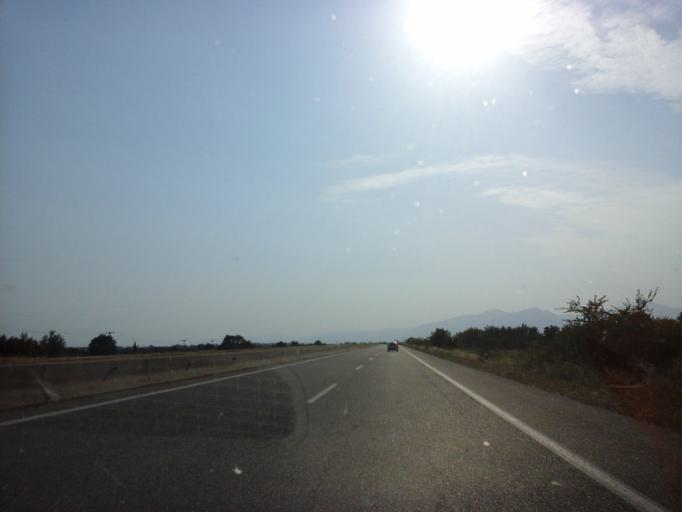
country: GR
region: East Macedonia and Thrace
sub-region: Nomos Xanthis
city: Selero
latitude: 41.1196
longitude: 25.0499
